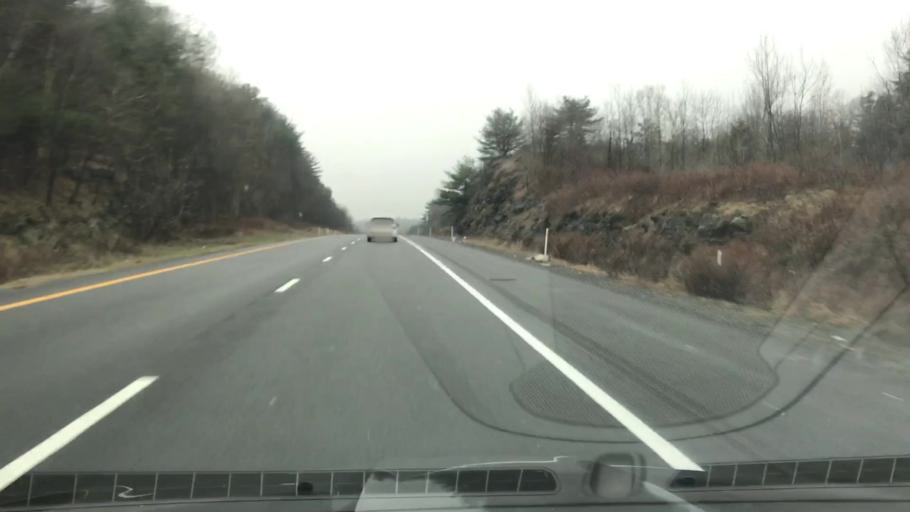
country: US
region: Pennsylvania
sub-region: Pike County
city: Hemlock Farms
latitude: 41.3584
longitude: -75.0570
